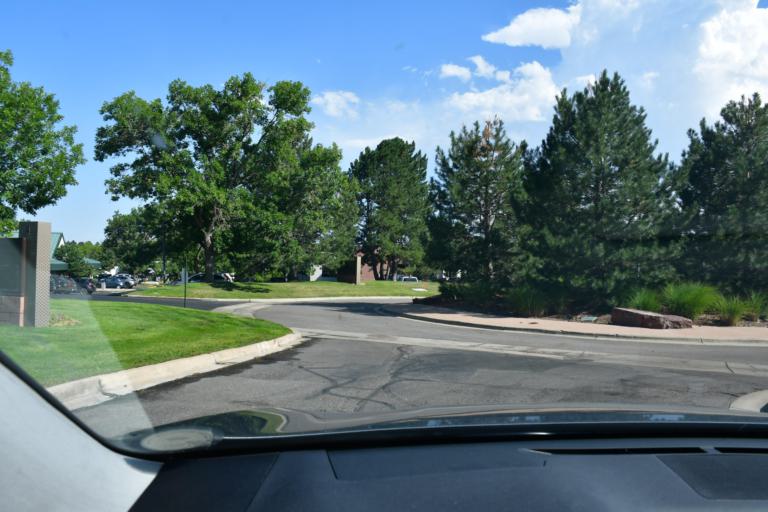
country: US
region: Colorado
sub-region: Douglas County
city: Meridian
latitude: 39.5681
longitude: -104.8636
